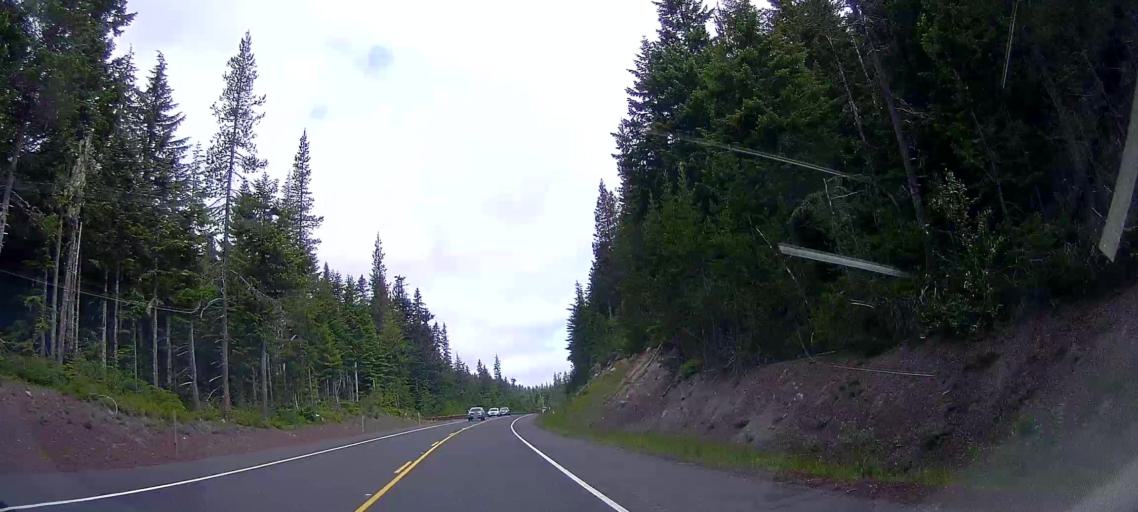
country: US
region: Oregon
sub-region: Clackamas County
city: Mount Hood Village
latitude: 45.2656
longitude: -121.7167
